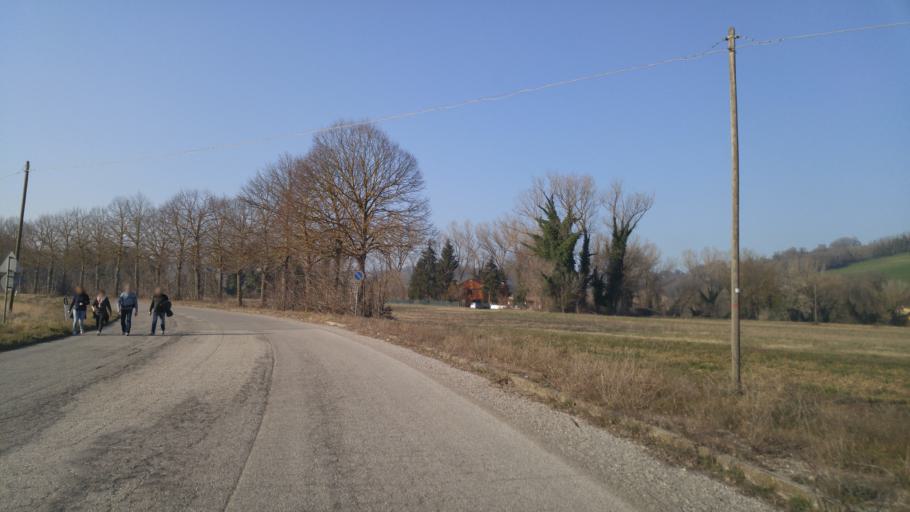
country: IT
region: The Marches
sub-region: Provincia di Pesaro e Urbino
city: Fenile
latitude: 43.8305
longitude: 12.9165
